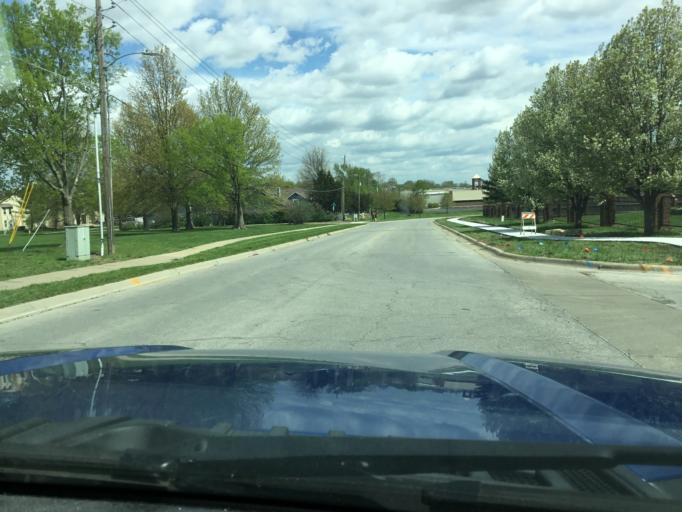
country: US
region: Kansas
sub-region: Douglas County
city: Lawrence
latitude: 38.9353
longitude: -95.2664
